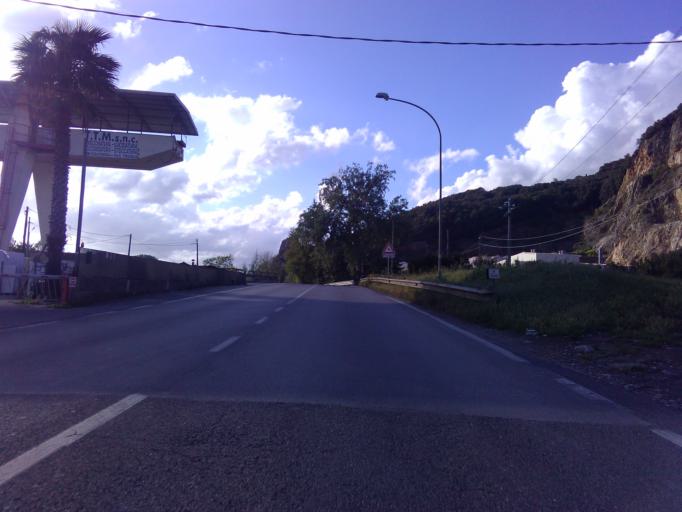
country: IT
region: Tuscany
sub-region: Provincia di Lucca
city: Strettoia
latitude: 43.9934
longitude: 10.1793
